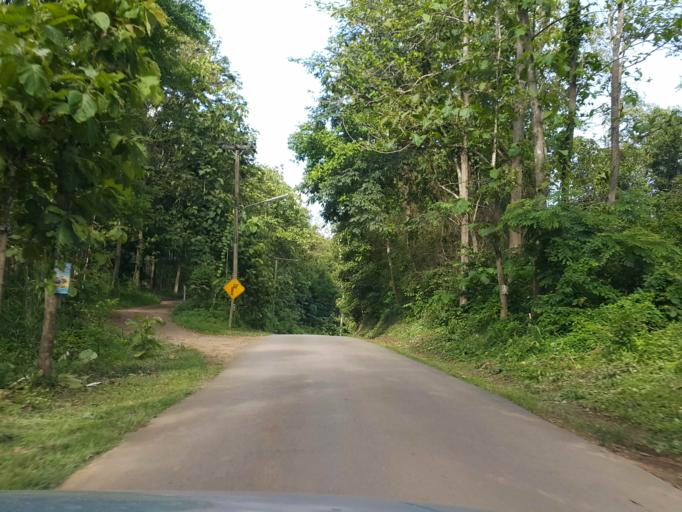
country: TH
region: Chiang Mai
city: Mae Taeng
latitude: 18.9663
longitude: 98.9010
